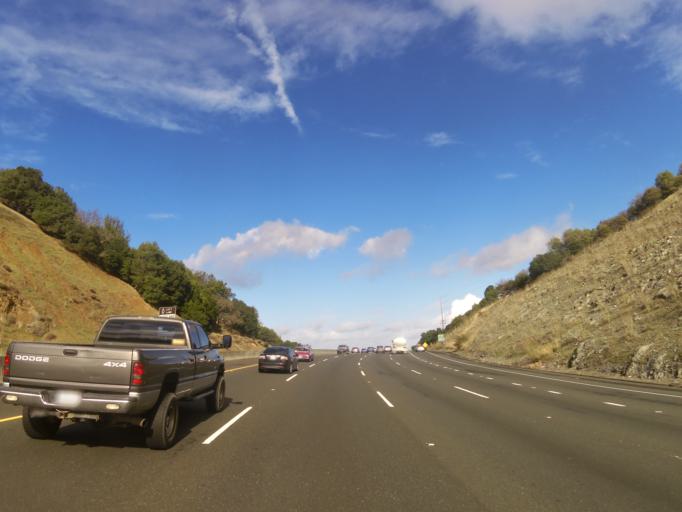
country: US
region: California
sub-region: Marin County
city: Lucas Valley-Marinwood
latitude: 38.0414
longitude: -122.5366
